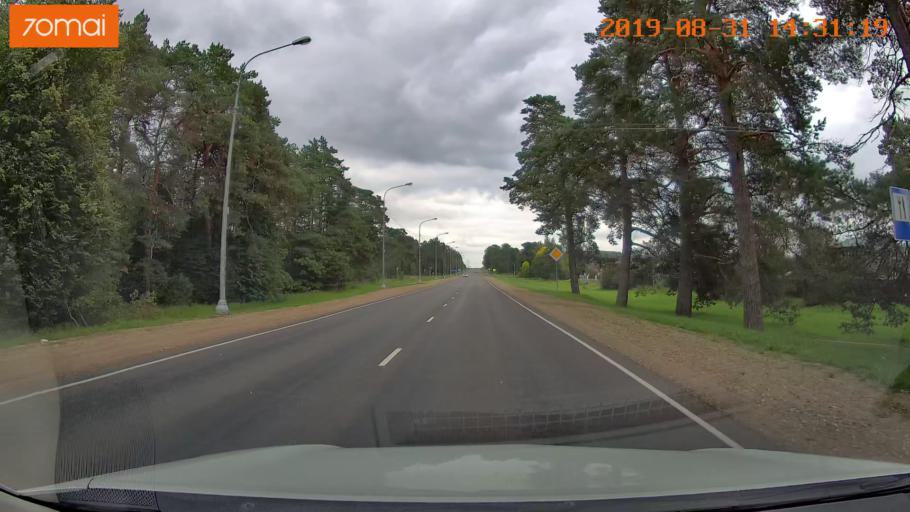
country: RU
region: Smolensk
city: Yekimovichi
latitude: 54.1374
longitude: 33.3705
